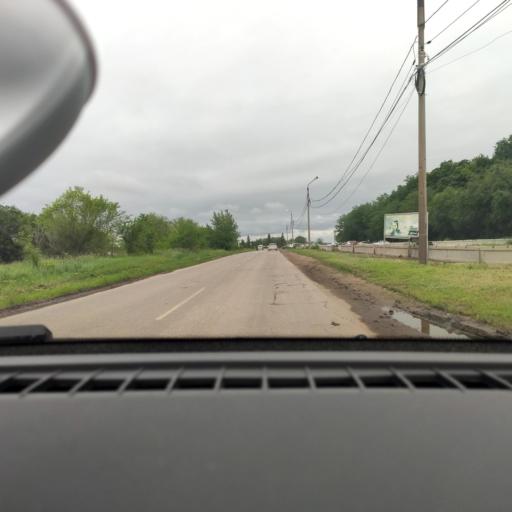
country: RU
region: Samara
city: Spiridonovka
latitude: 53.0552
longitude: 50.4886
